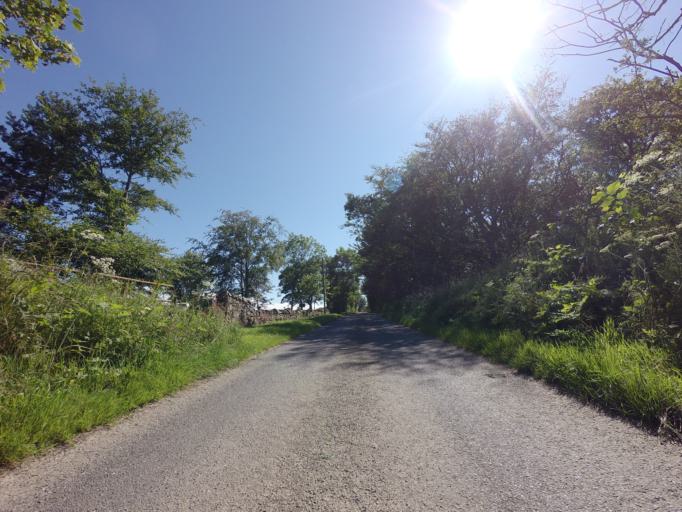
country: GB
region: Scotland
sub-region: Aberdeenshire
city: Macduff
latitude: 57.6508
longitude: -2.5033
